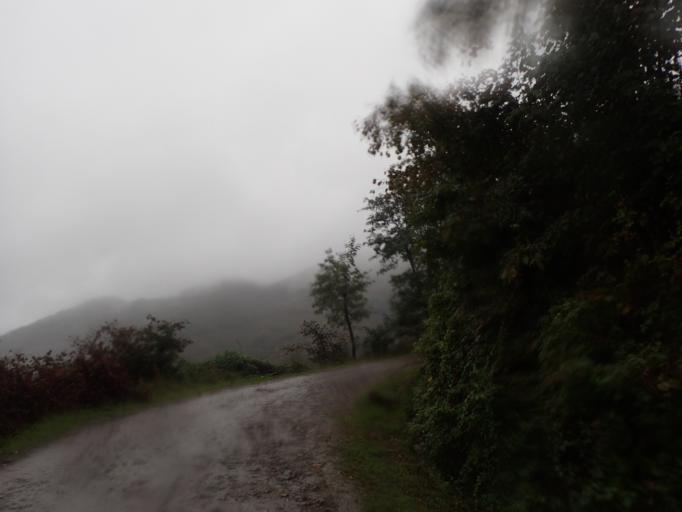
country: TR
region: Ordu
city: Persembe
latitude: 41.0329
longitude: 37.7237
